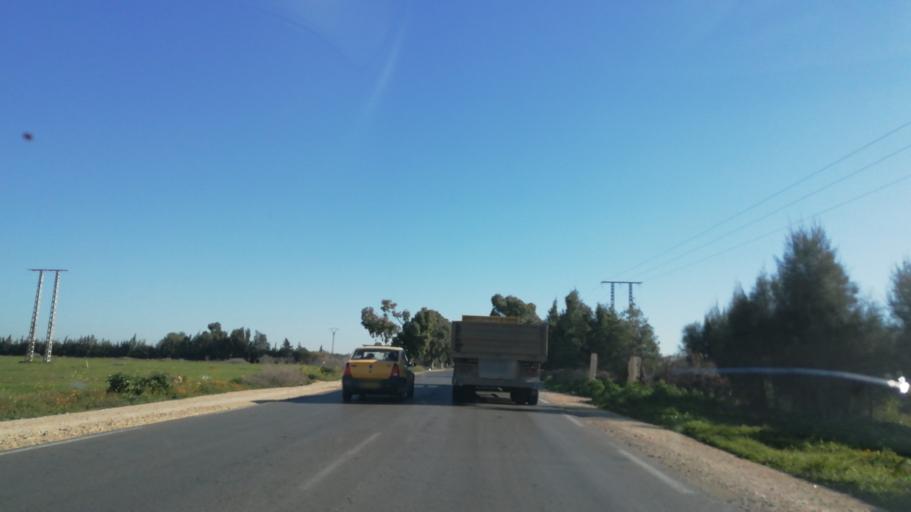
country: DZ
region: Relizane
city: Zemoura
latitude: 35.7485
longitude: 0.6922
